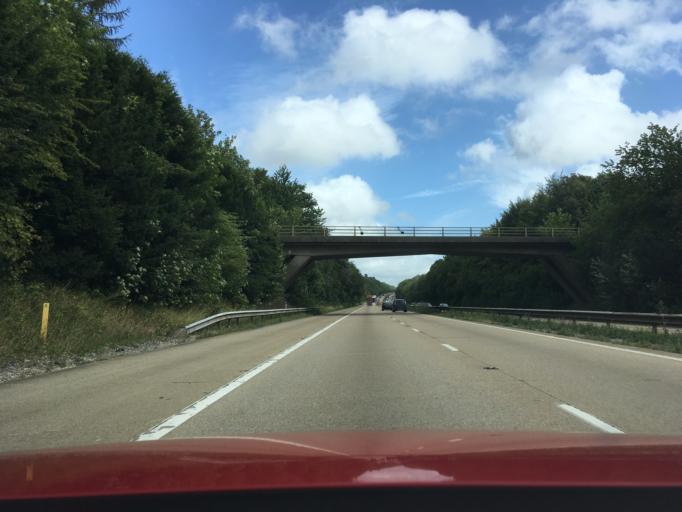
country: GB
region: England
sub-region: Hampshire
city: Kings Worthy
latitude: 51.1560
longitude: -1.2372
